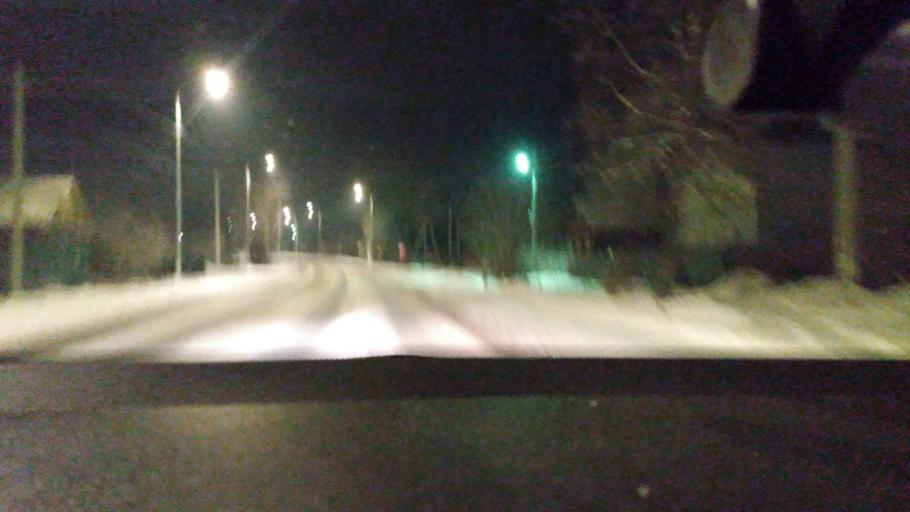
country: RU
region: Moskovskaya
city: Krasnaya Poyma
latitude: 55.1005
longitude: 38.9874
